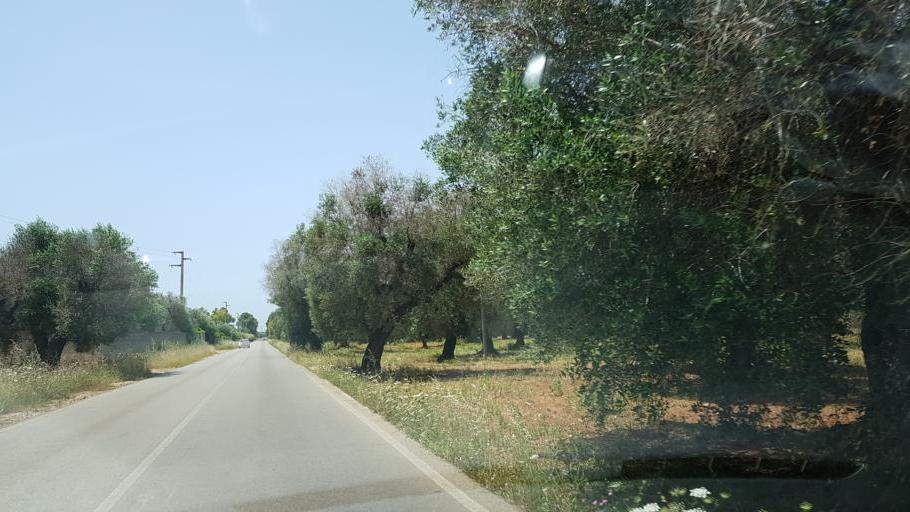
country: IT
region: Apulia
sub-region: Provincia di Lecce
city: Veglie
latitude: 40.3246
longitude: 17.9156
